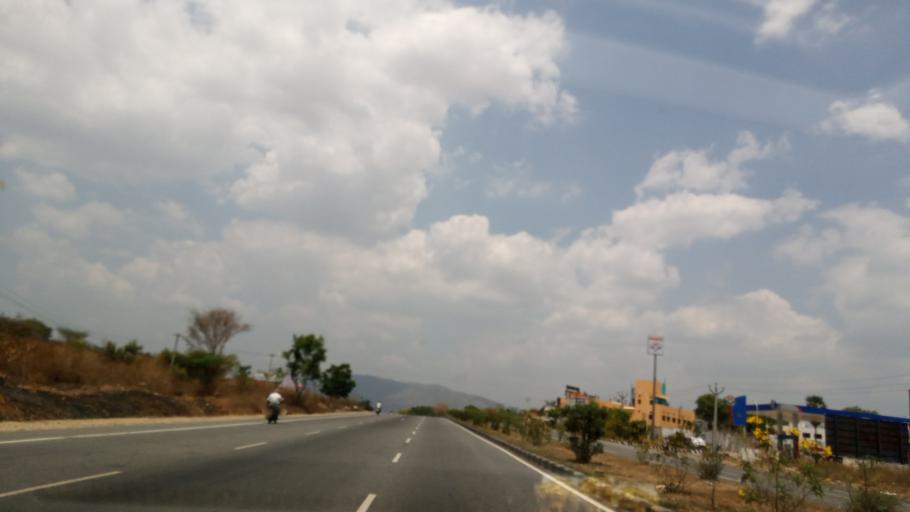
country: IN
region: Tamil Nadu
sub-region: Vellore
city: Vaniyambadi
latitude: 12.6550
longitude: 78.6006
